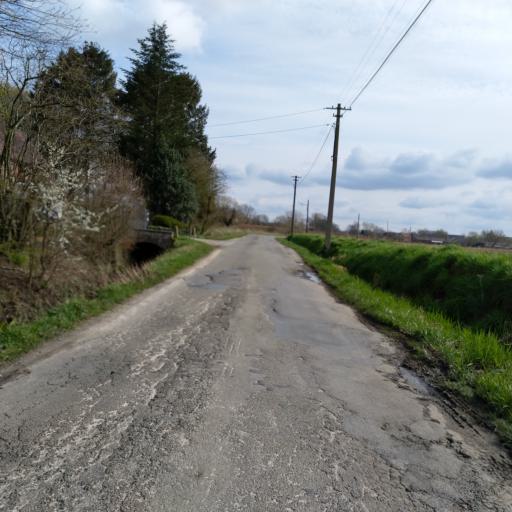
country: BE
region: Wallonia
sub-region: Province du Hainaut
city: Soignies
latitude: 50.5318
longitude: 4.0564
